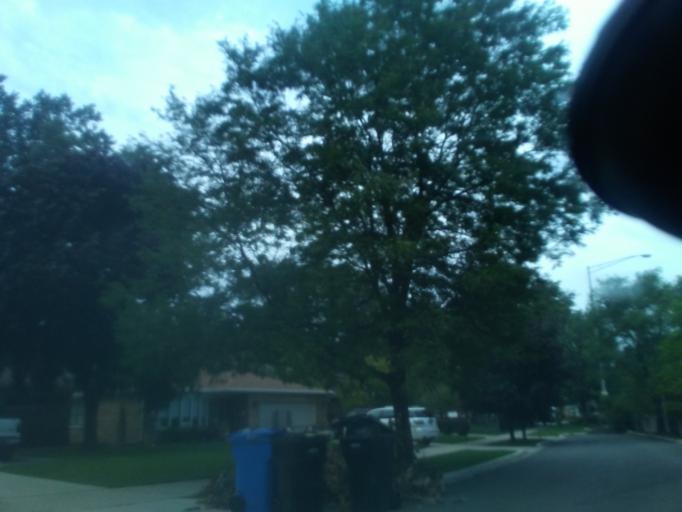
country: US
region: Illinois
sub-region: Cook County
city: Lincolnwood
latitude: 41.9900
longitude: -87.7536
